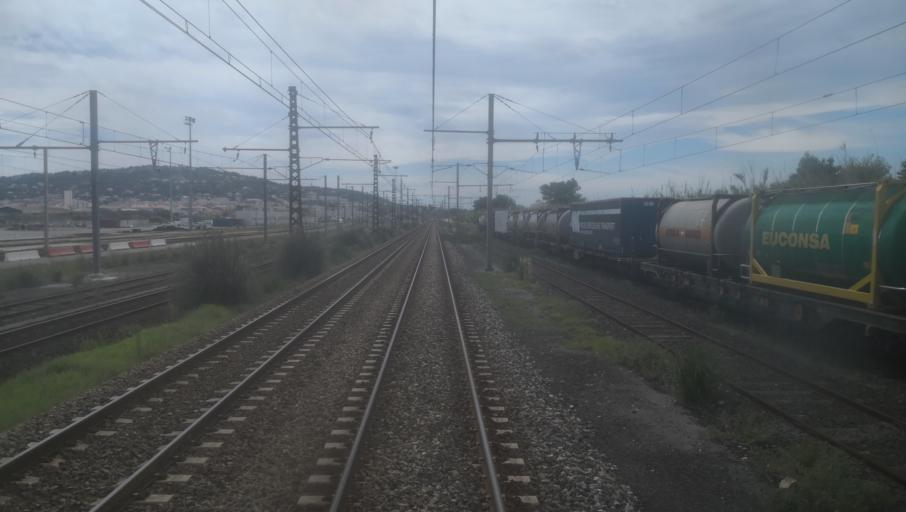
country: FR
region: Languedoc-Roussillon
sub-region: Departement de l'Herault
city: Sete
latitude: 43.4161
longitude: 3.7125
